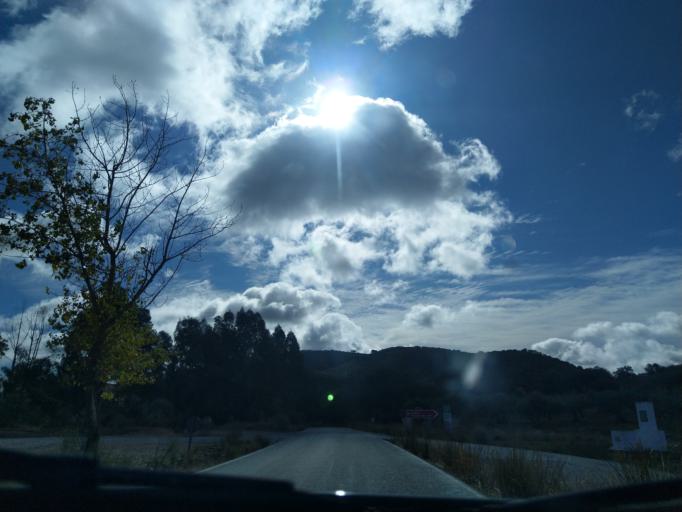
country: ES
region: Extremadura
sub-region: Provincia de Badajoz
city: Reina
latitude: 38.1263
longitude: -5.9140
